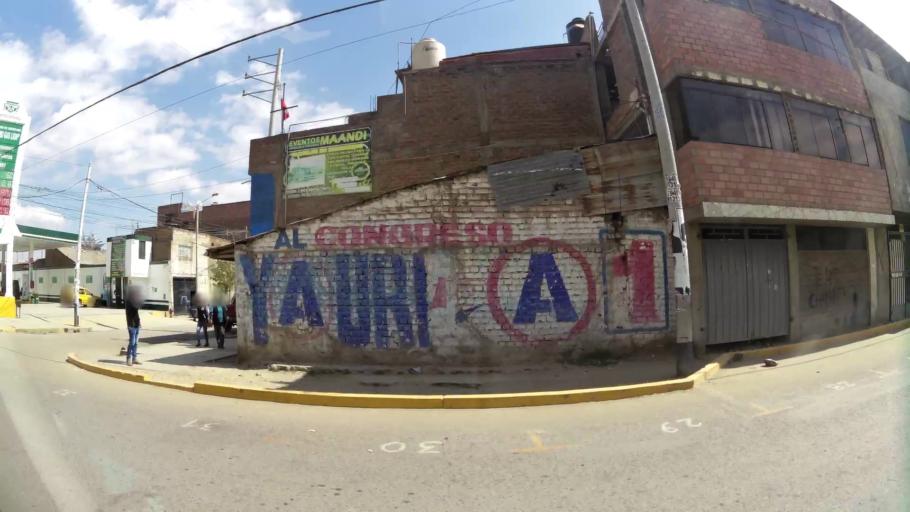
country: PE
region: Junin
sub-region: Provincia de Huancayo
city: Huancayo
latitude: -12.0810
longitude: -75.1982
